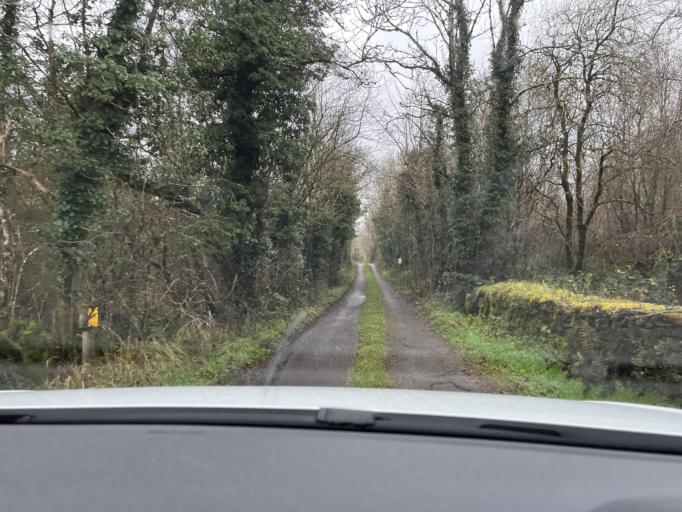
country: IE
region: Connaught
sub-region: County Leitrim
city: Manorhamilton
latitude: 54.2845
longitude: -8.1156
